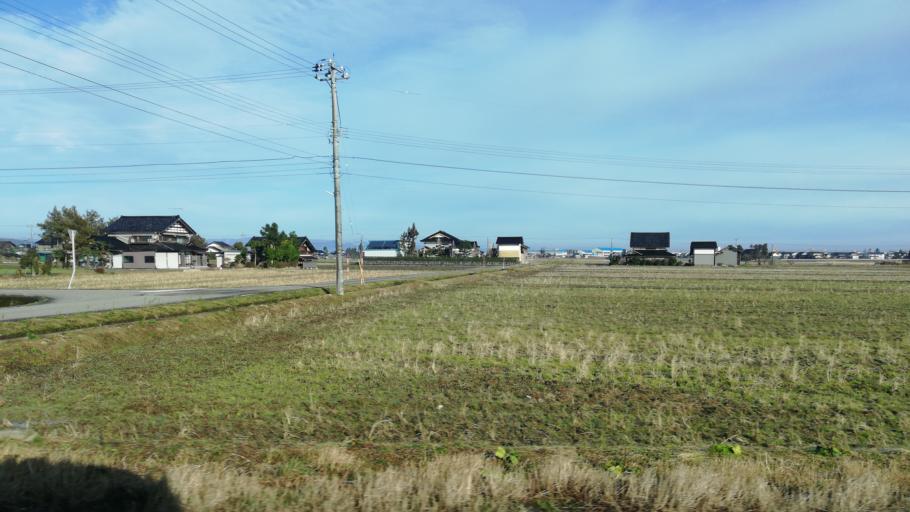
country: JP
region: Toyama
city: Nanto-shi
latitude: 36.5742
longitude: 136.9184
